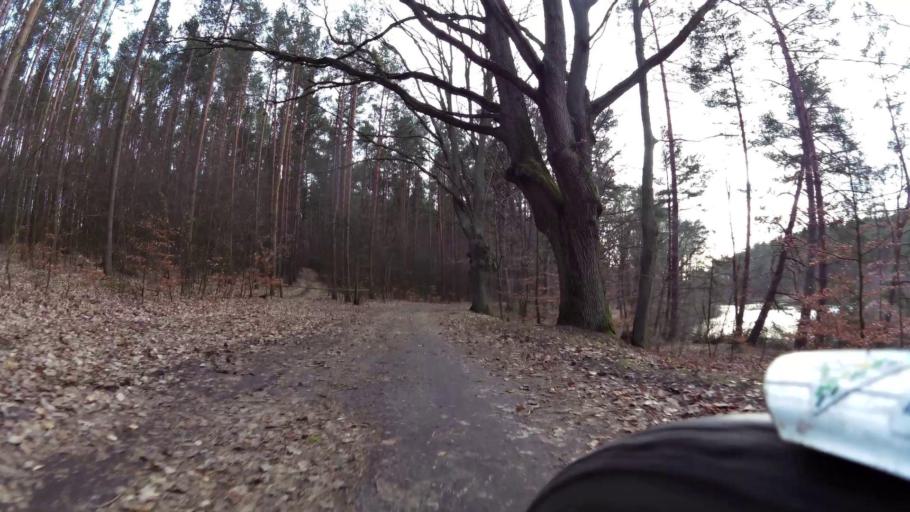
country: PL
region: West Pomeranian Voivodeship
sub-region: Powiat kamienski
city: Wolin
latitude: 53.9689
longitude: 14.5871
